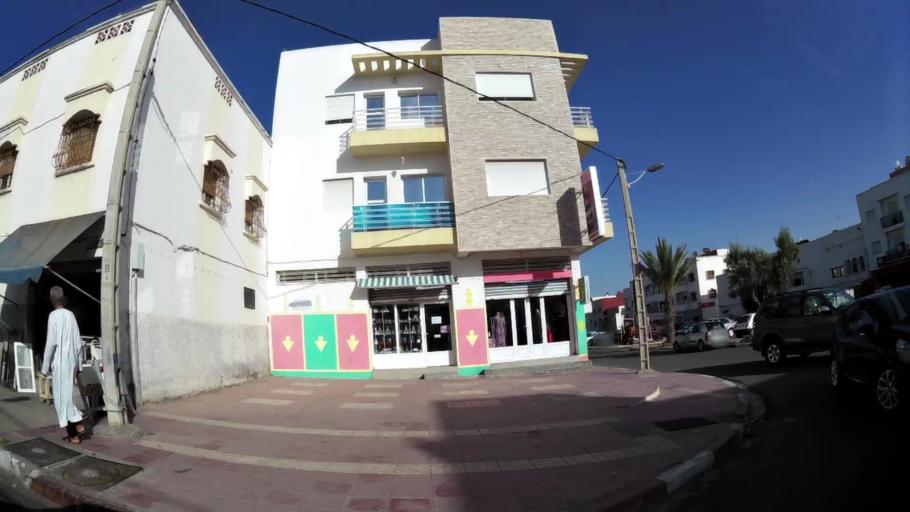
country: MA
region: Souss-Massa-Draa
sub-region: Agadir-Ida-ou-Tnan
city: Agadir
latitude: 30.4252
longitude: -9.5836
